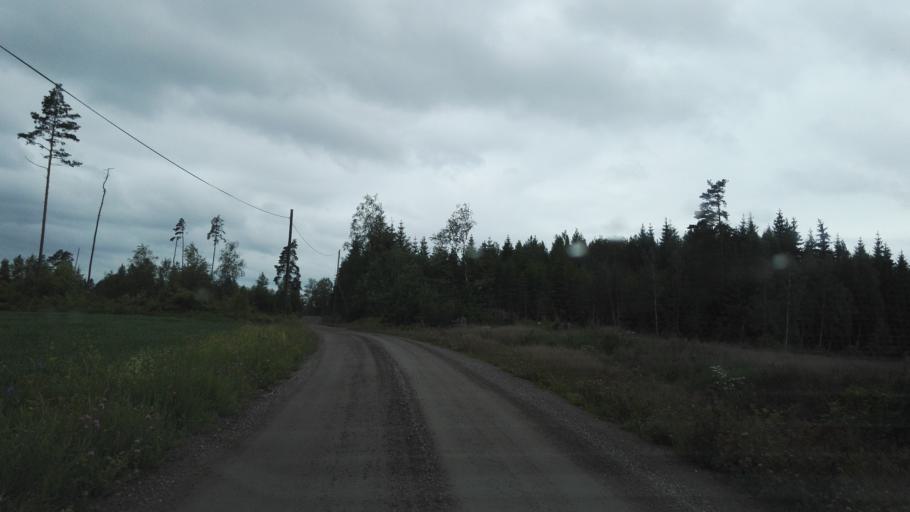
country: SE
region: Joenkoeping
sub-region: Vetlanda Kommun
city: Landsbro
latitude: 57.3214
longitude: 14.8833
